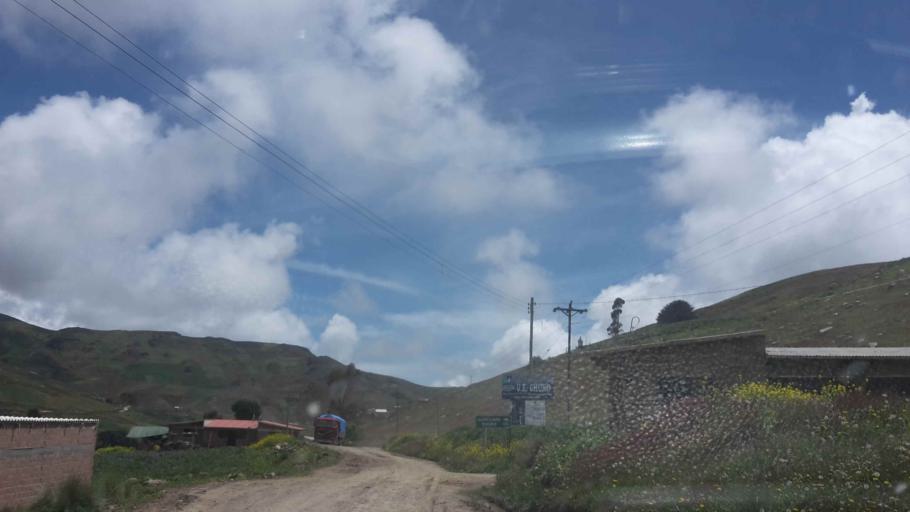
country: BO
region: Cochabamba
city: Cochabamba
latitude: -17.1967
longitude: -66.0825
